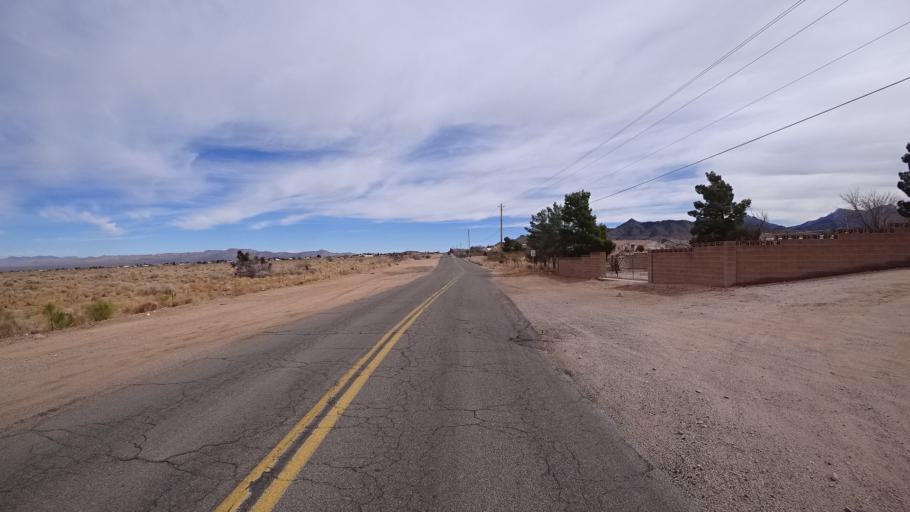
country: US
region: Arizona
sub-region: Mohave County
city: Kingman
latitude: 35.1958
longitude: -113.9860
